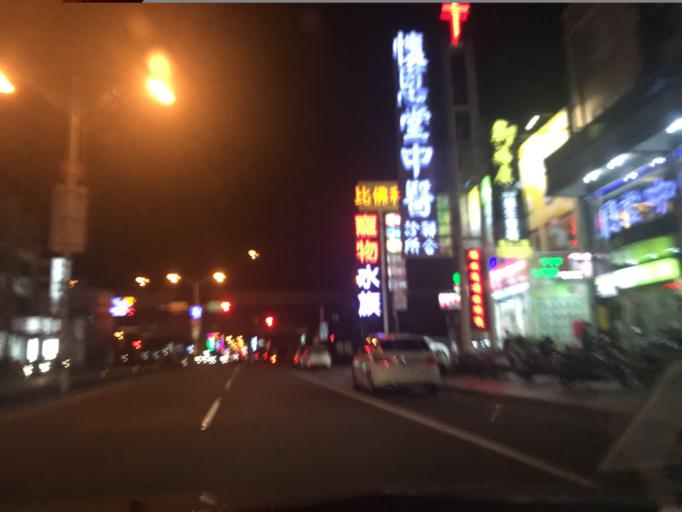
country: TW
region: Taiwan
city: Daxi
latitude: 24.8616
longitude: 121.2177
